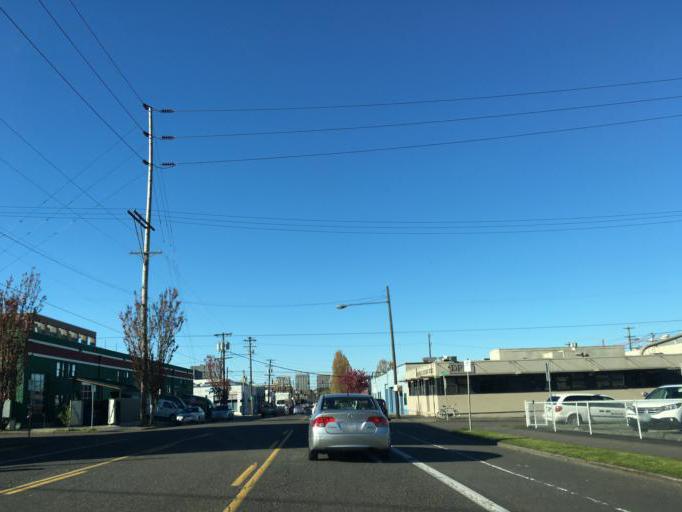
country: US
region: Oregon
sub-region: Multnomah County
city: Portland
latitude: 45.5105
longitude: -122.6587
